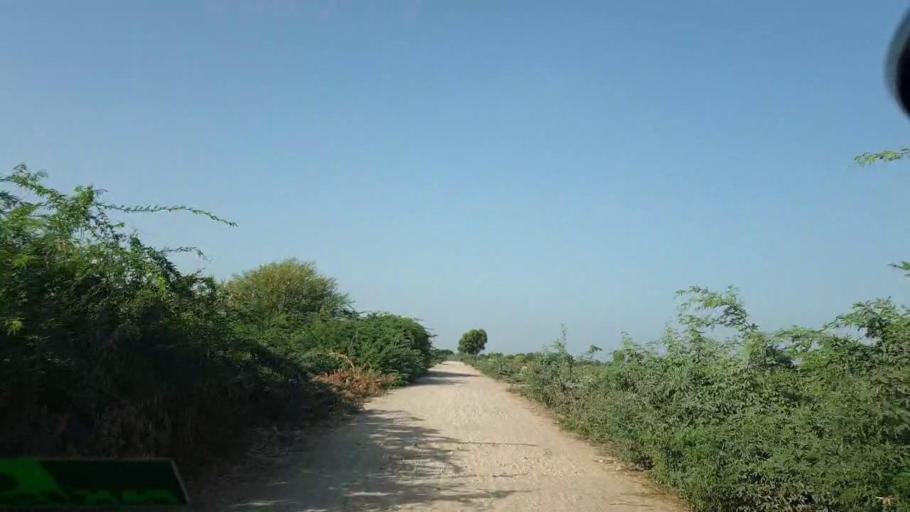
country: PK
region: Sindh
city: Naukot
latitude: 24.7388
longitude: 69.2198
